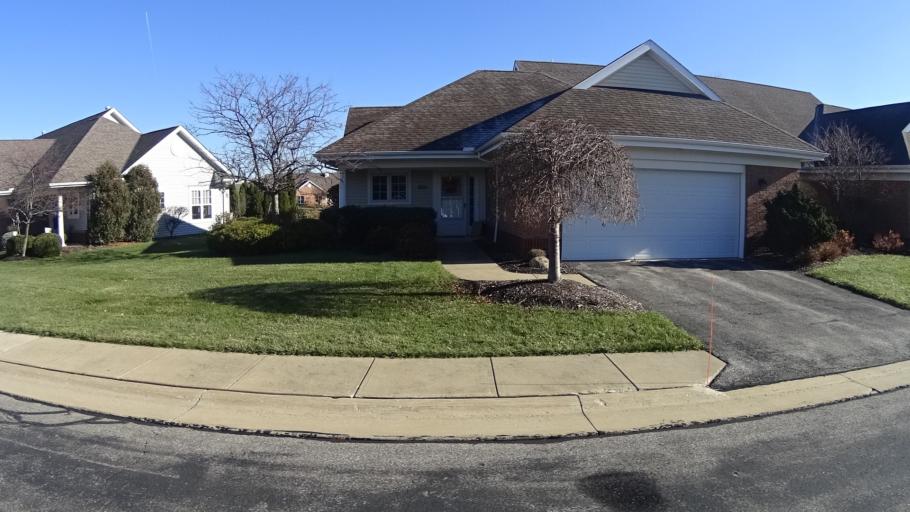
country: US
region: Ohio
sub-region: Lorain County
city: Sheffield
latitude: 41.4223
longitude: -82.0728
